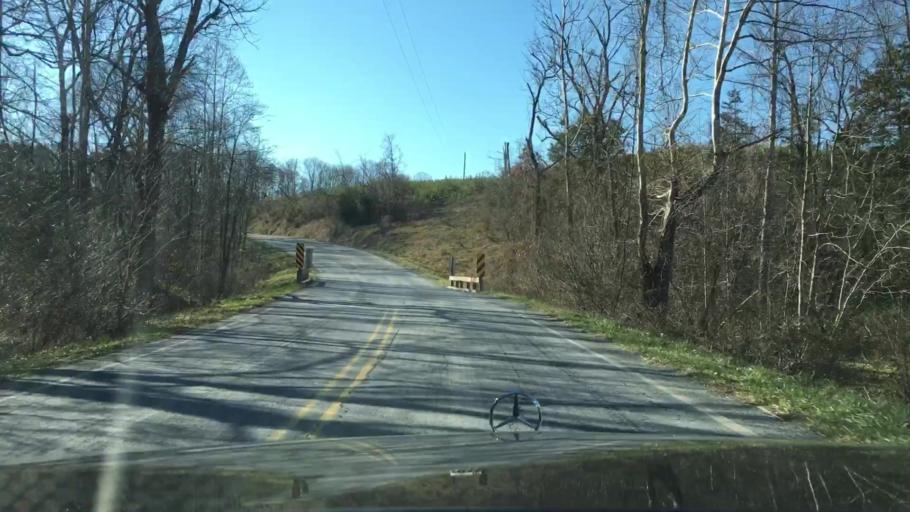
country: US
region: Virginia
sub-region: Pittsylvania County
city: Motley
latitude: 37.1544
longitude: -79.3845
